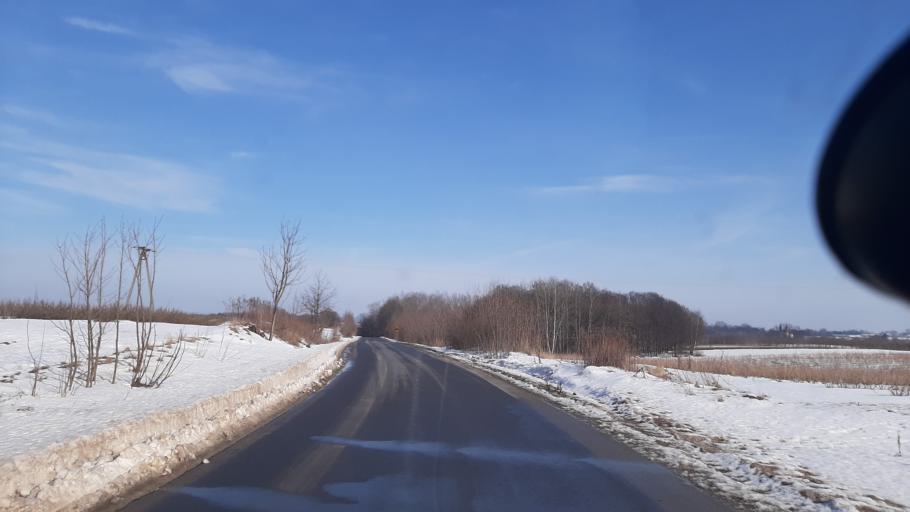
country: PL
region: Lublin Voivodeship
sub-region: Powiat pulawski
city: Wawolnica
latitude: 51.3517
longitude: 22.1158
